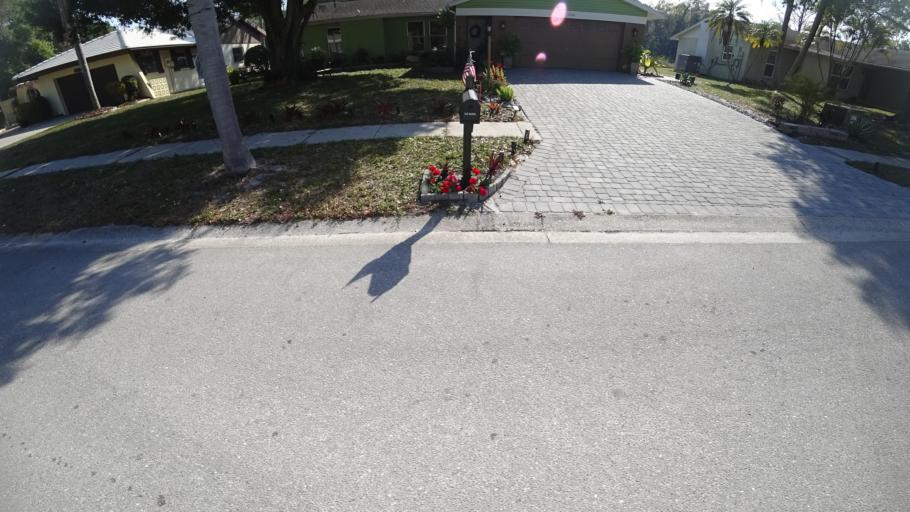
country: US
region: Florida
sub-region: Manatee County
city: Whitfield
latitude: 27.4107
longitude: -82.5514
